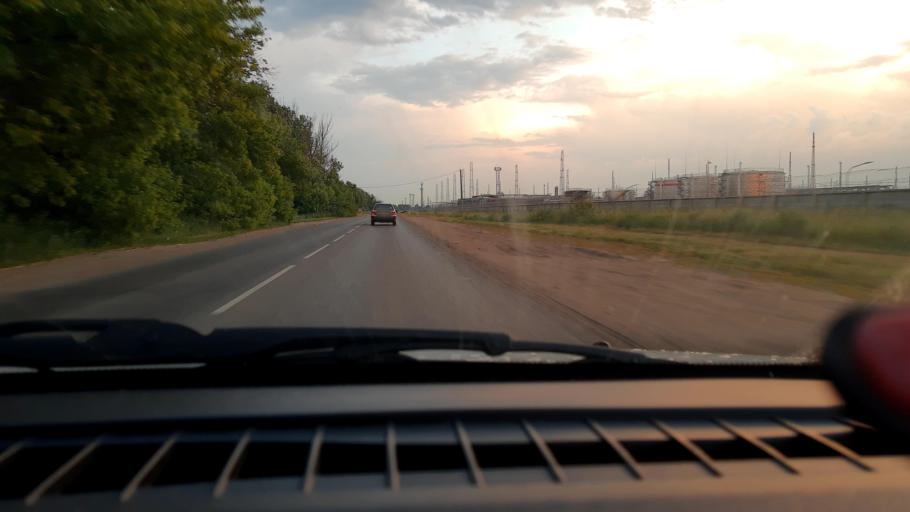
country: RU
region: Nizjnij Novgorod
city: Kstovo
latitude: 56.1240
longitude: 44.1282
